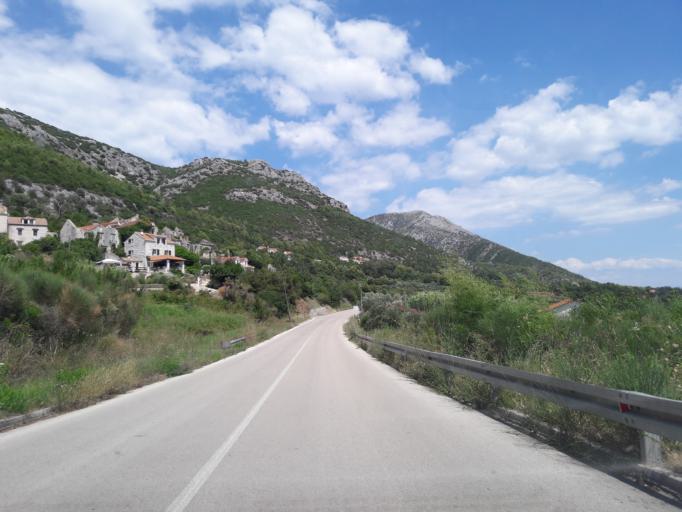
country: HR
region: Dubrovacko-Neretvanska
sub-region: Grad Korcula
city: Zrnovo
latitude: 42.9863
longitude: 17.0910
